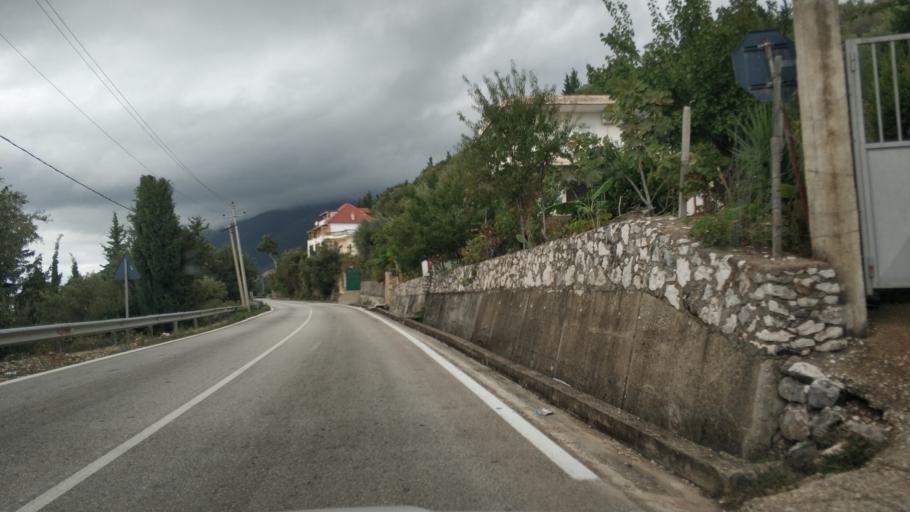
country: AL
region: Vlore
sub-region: Rrethi i Vlores
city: Vranisht
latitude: 40.1625
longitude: 19.6233
